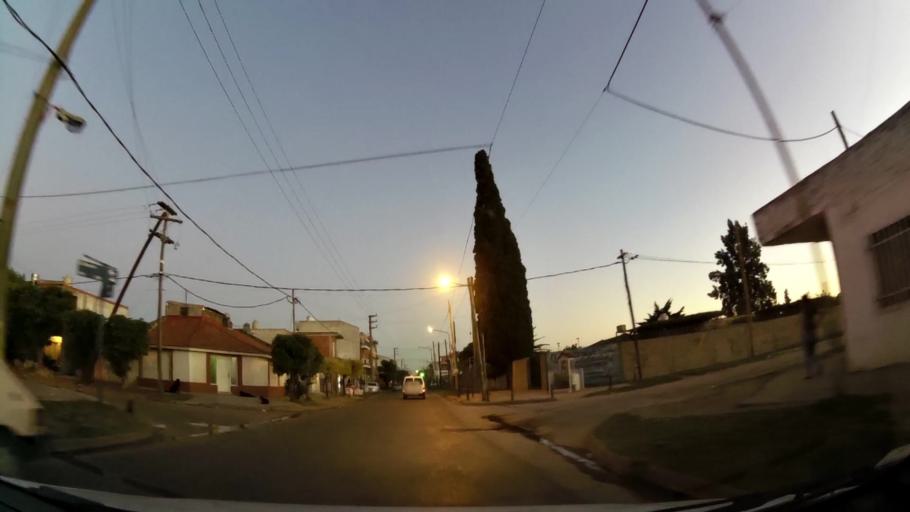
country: AR
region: Buenos Aires
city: San Justo
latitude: -34.7074
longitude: -58.6005
